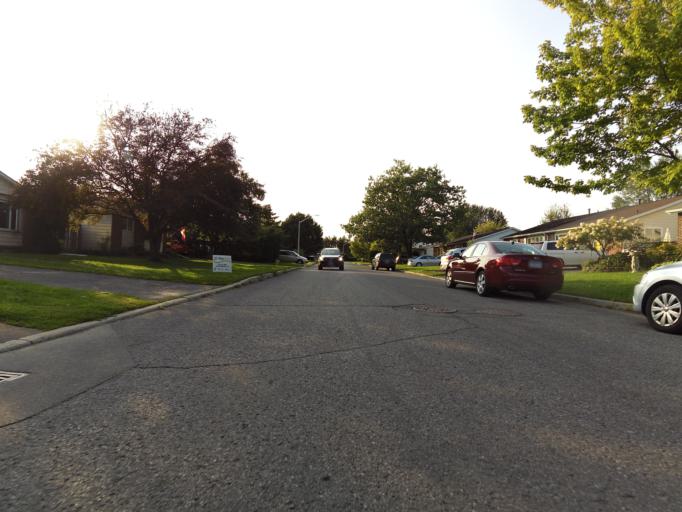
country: CA
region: Ontario
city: Bells Corners
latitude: 45.2898
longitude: -75.8751
